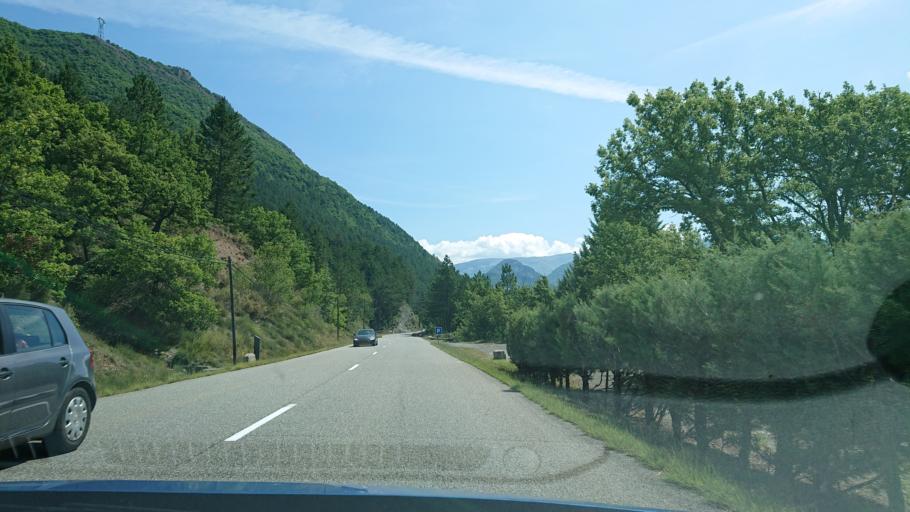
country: FR
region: Provence-Alpes-Cote d'Azur
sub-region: Departement des Alpes-de-Haute-Provence
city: Sisteron
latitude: 44.2664
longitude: 5.9862
